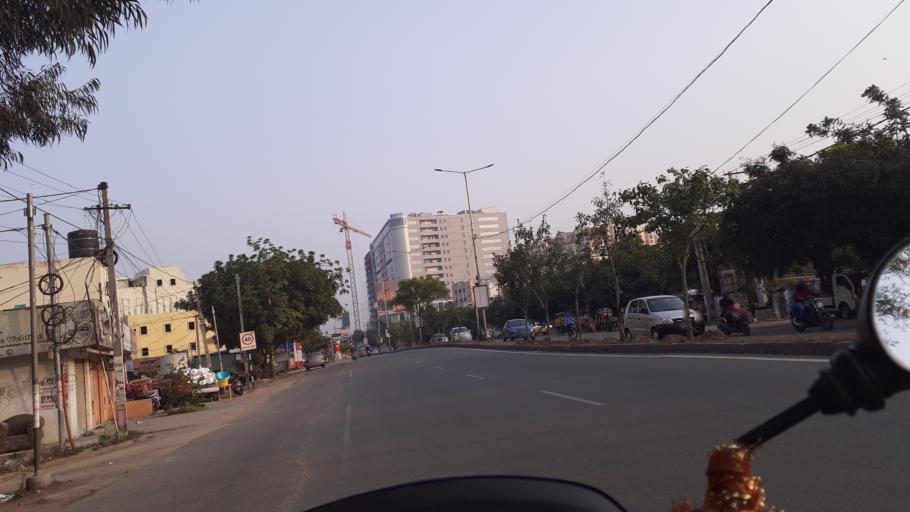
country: IN
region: Telangana
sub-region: Medak
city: Serilingampalle
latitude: 17.4879
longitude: 78.3560
